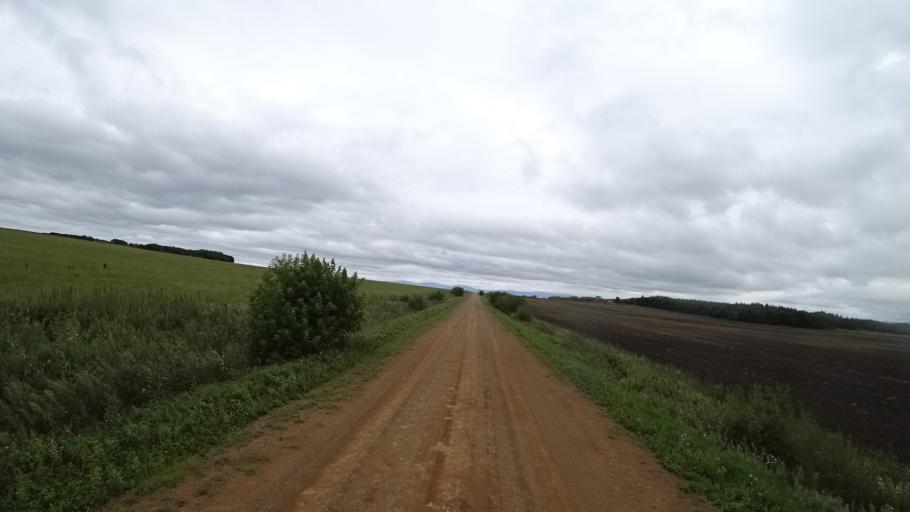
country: RU
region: Primorskiy
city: Chernigovka
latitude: 44.4361
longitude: 132.5864
